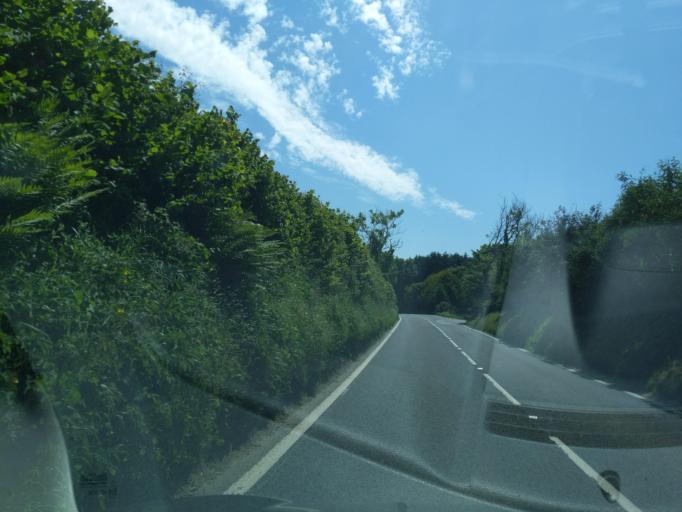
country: GB
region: England
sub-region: Cornwall
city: Camelford
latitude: 50.6096
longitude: -4.6897
